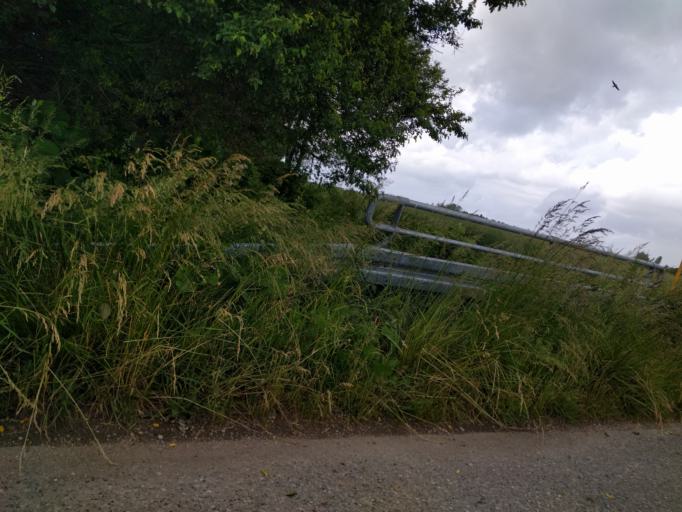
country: DK
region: South Denmark
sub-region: Kerteminde Kommune
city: Munkebo
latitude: 55.4611
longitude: 10.5160
